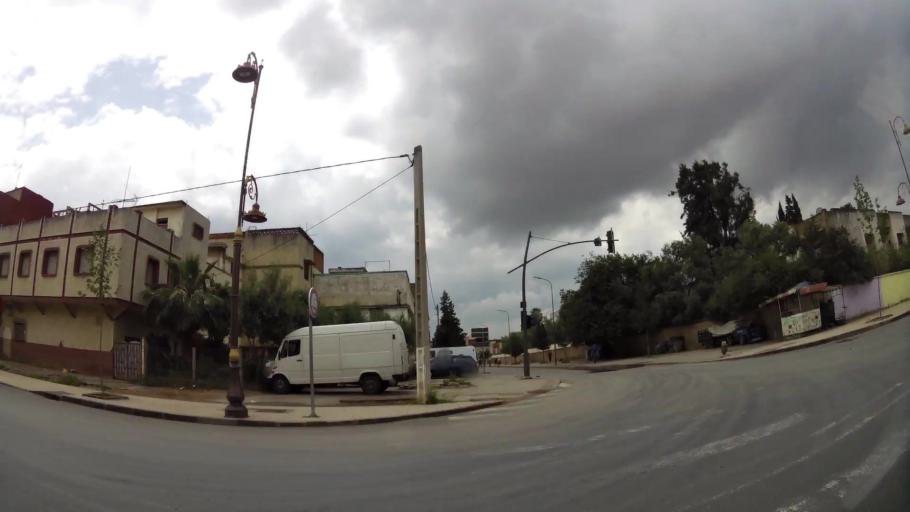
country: MA
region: Rabat-Sale-Zemmour-Zaer
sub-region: Khemisset
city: Tiflet
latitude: 33.8875
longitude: -6.3169
